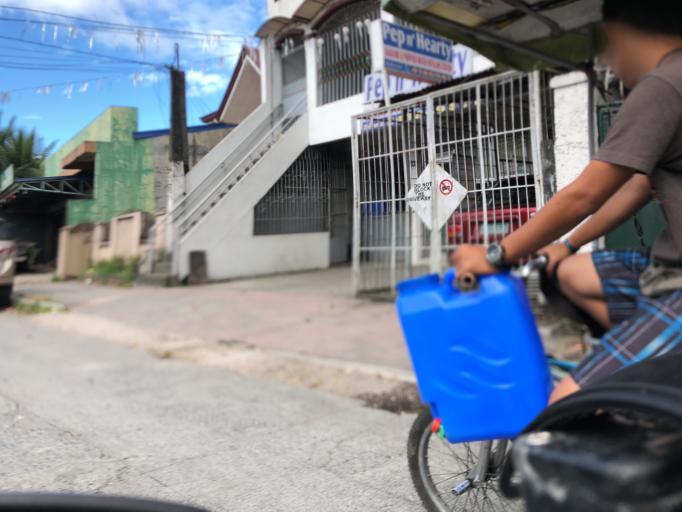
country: PH
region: Central Luzon
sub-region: Province of Bulacan
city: San Jose del Monte
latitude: 14.7391
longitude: 121.0568
